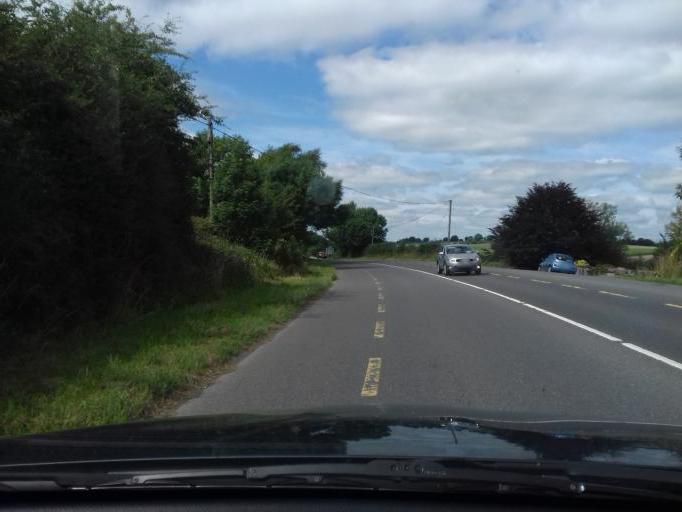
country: IE
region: Leinster
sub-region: Wicklow
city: Baltinglass
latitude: 53.0087
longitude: -6.6417
